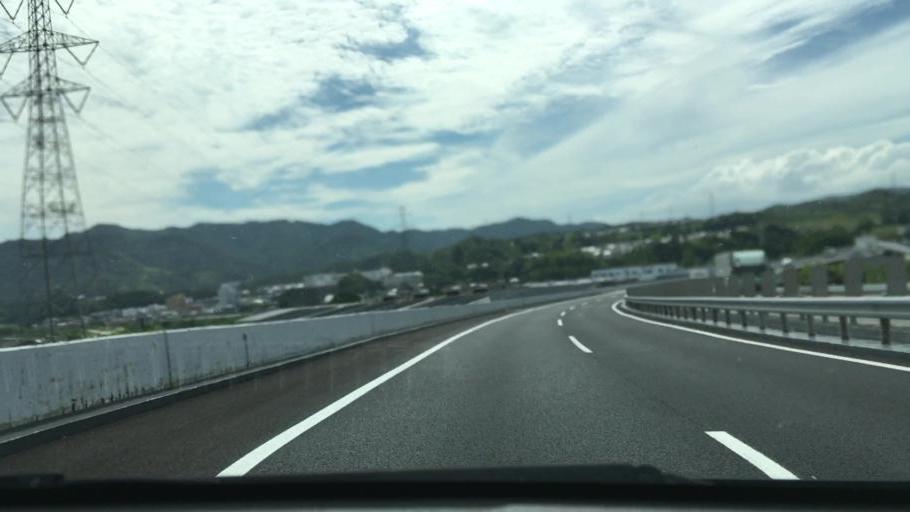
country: JP
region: Yamaguchi
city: Ogori-shimogo
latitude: 34.1226
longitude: 131.4149
